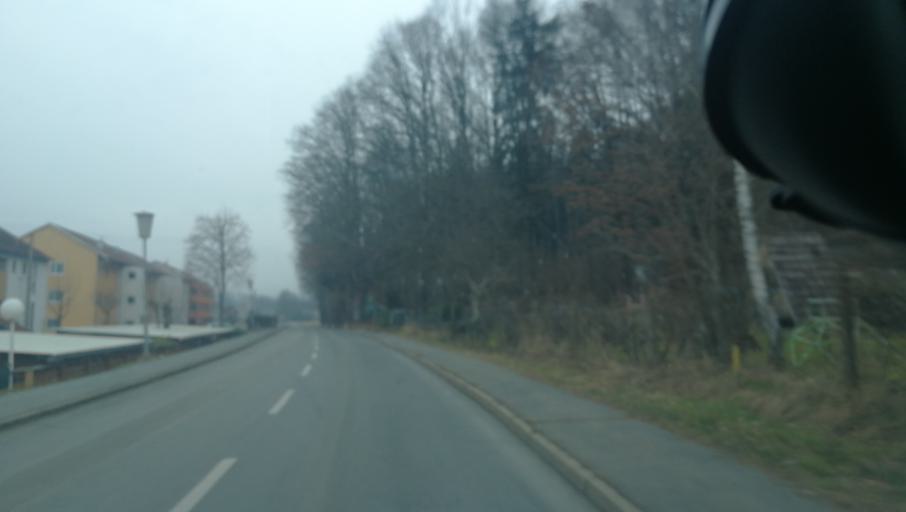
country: AT
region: Styria
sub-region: Politischer Bezirk Deutschlandsberg
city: Stainz
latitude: 46.8984
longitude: 15.2528
